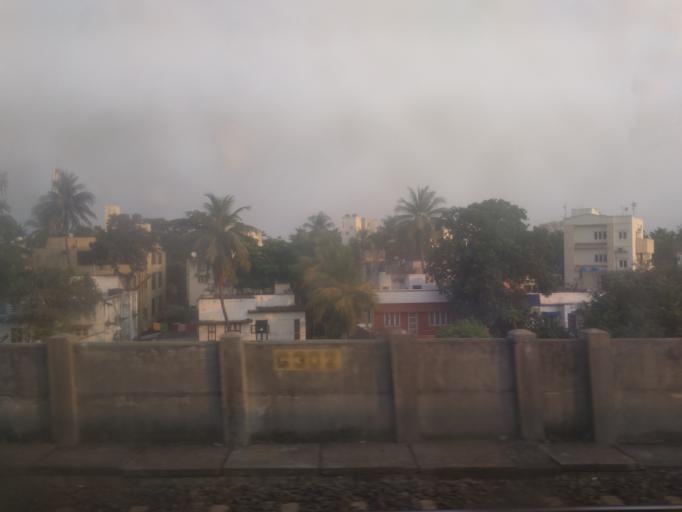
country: IN
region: Tamil Nadu
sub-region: Chennai
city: Gandhi Nagar
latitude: 13.0332
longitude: 80.2643
